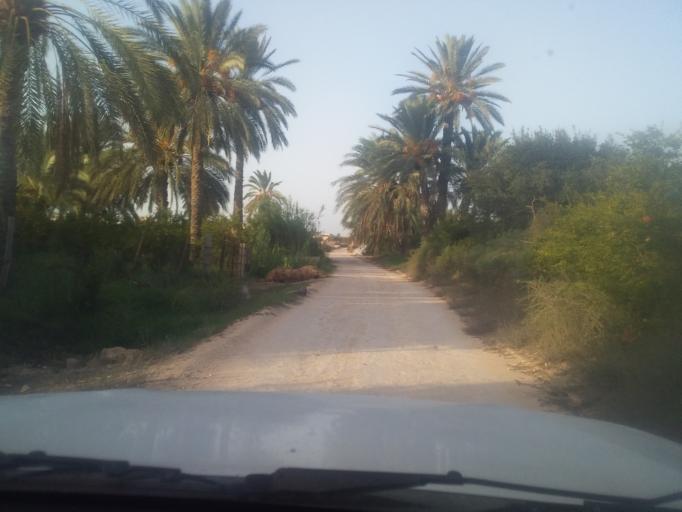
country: TN
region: Qabis
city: Gabes
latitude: 33.6302
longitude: 10.2911
